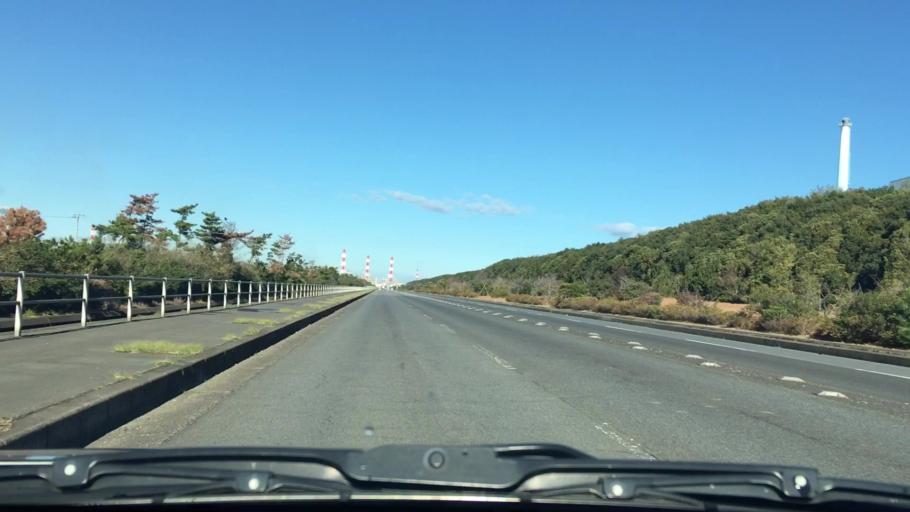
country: JP
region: Chiba
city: Omigawa
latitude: 35.8749
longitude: 140.7338
